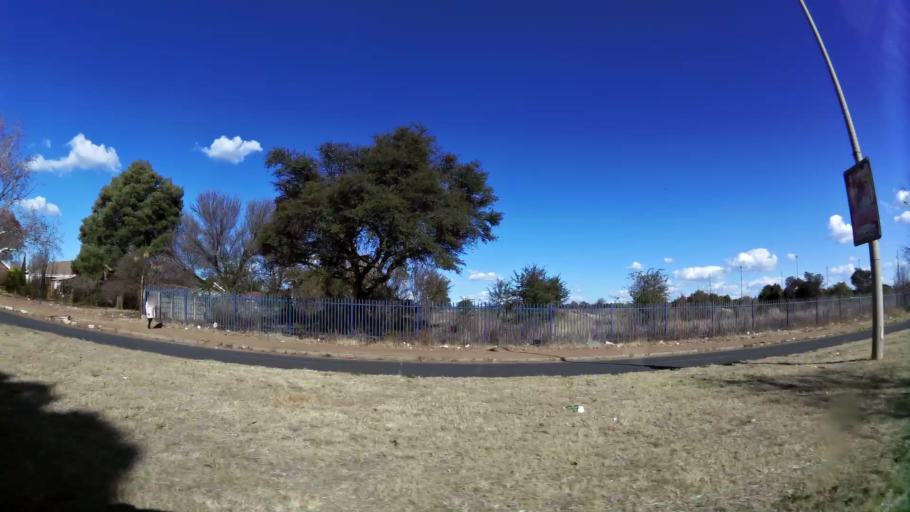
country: ZA
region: Gauteng
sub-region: West Rand District Municipality
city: Carletonville
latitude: -26.3584
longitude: 27.3858
